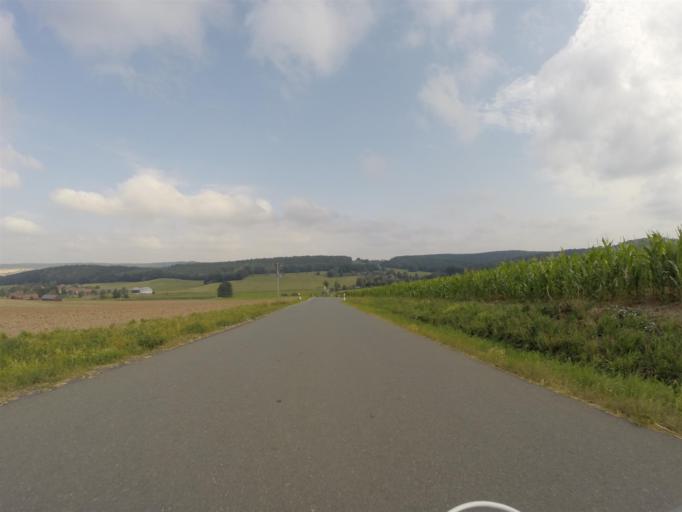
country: DE
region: Thuringia
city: Ruttersdorf-Lotschen
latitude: 50.8818
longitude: 11.7301
